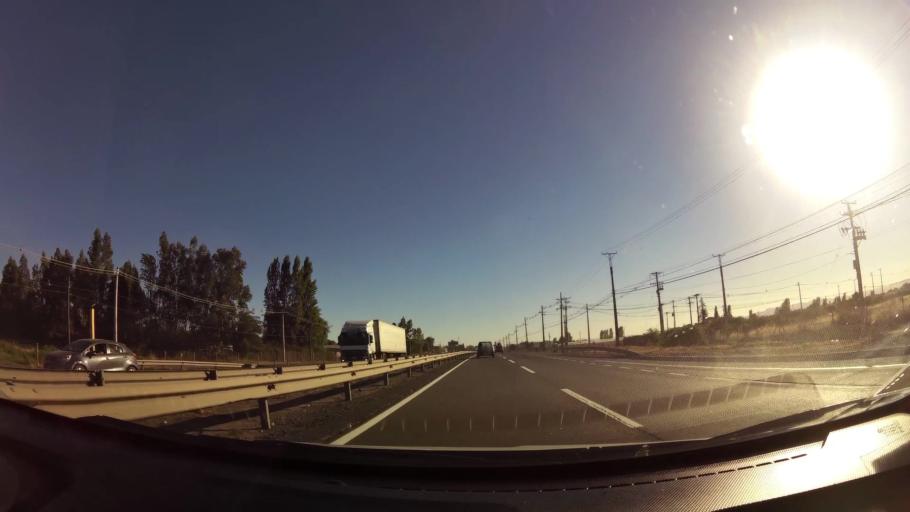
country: CL
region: Maule
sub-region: Provincia de Curico
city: Teno
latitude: -34.8704
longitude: -71.1376
